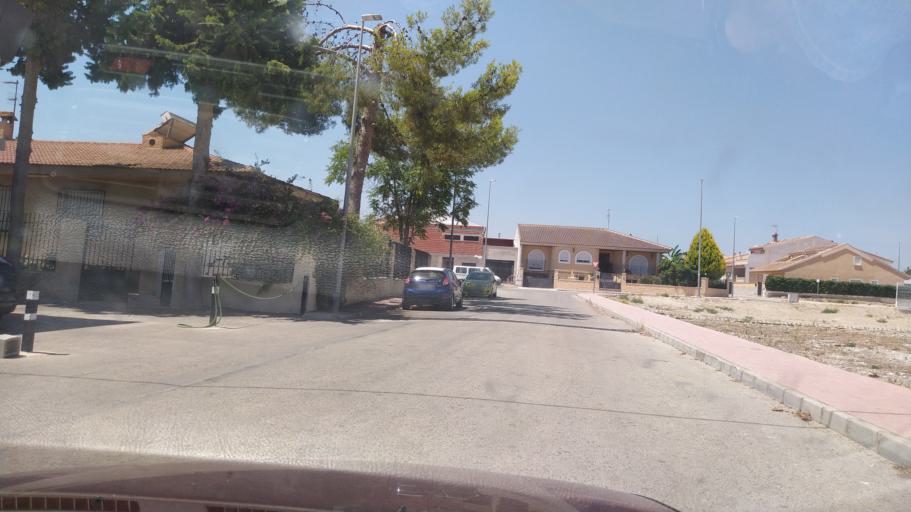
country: ES
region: Murcia
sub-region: Murcia
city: Ceuti
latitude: 38.0850
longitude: -1.2752
